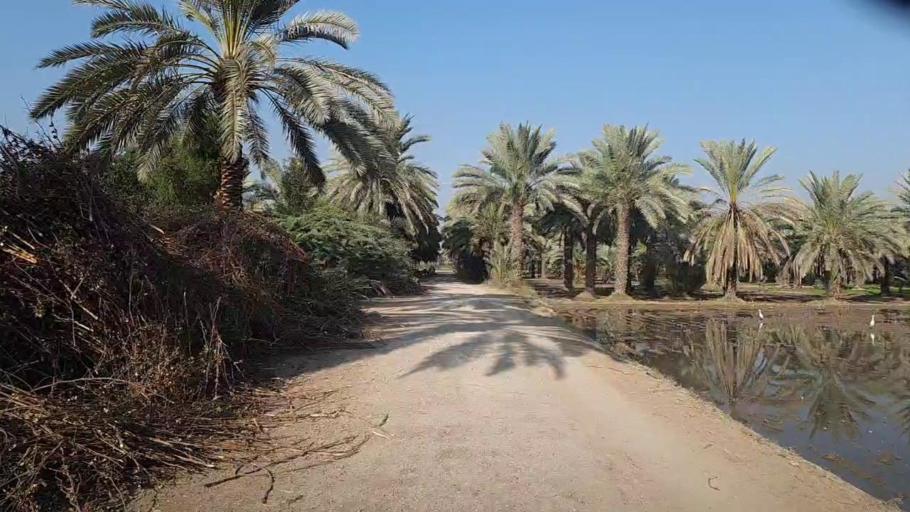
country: PK
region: Sindh
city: Ranipur
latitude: 27.2569
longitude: 68.5526
